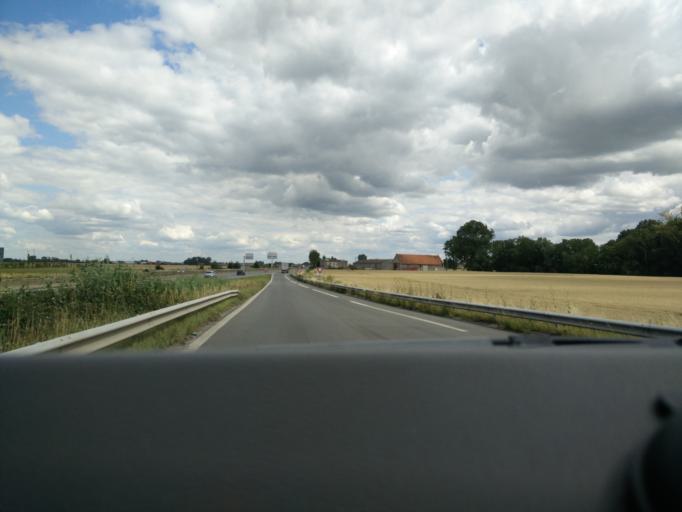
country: FR
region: Nord-Pas-de-Calais
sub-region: Departement du Nord
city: Socx
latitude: 50.9478
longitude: 2.4333
